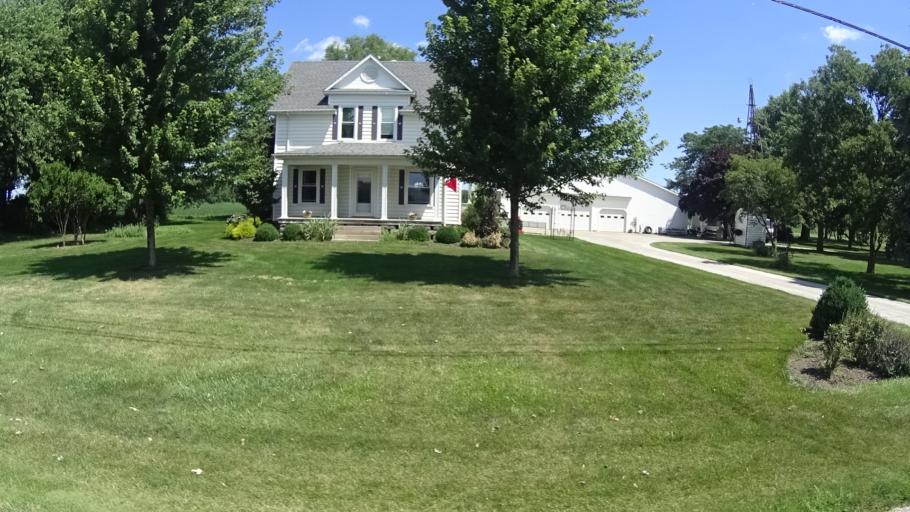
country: US
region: Ohio
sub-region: Erie County
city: Huron
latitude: 41.3891
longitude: -82.5807
